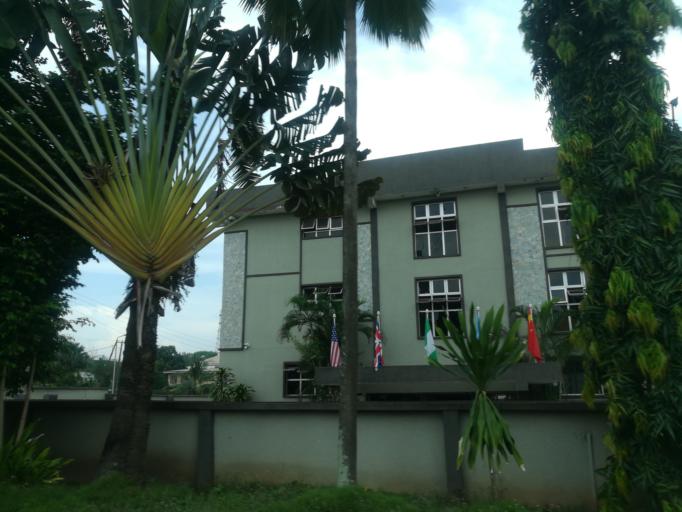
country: NG
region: Oyo
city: Ibadan
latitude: 7.4148
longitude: 3.9064
